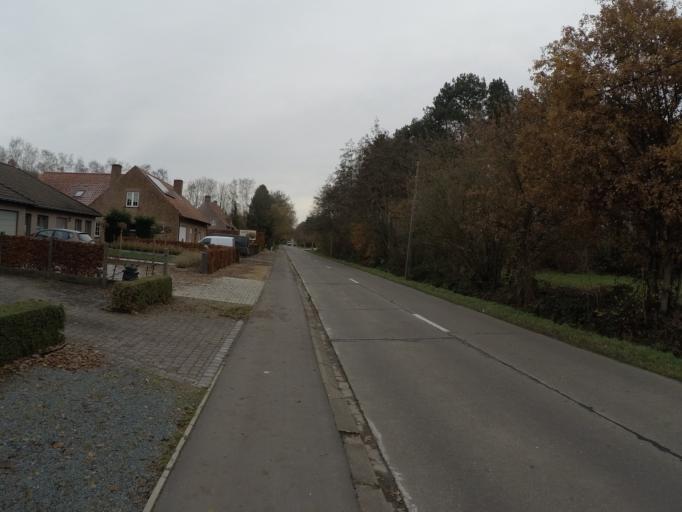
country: BE
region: Flanders
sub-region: Provincie Antwerpen
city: Berlaar
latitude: 51.1074
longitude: 4.6969
